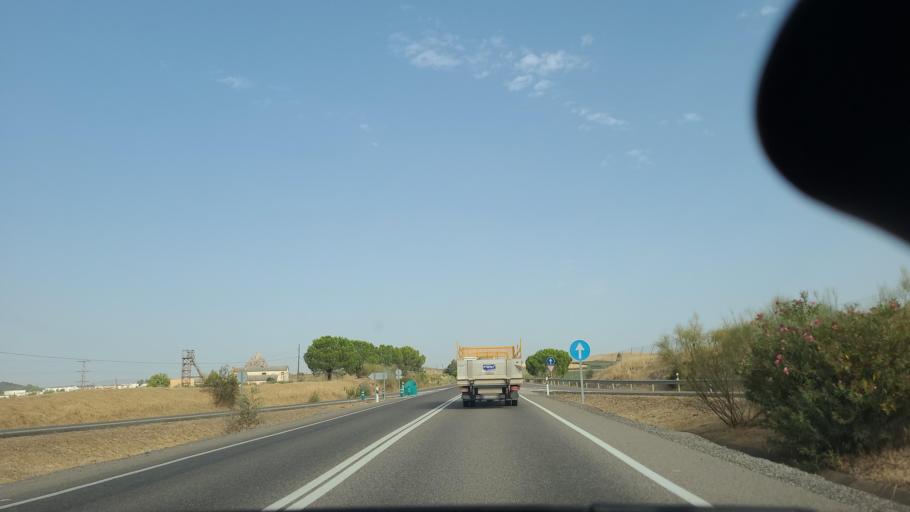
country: ES
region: Andalusia
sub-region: Province of Cordoba
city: Belmez
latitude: 38.2650
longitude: -5.1848
